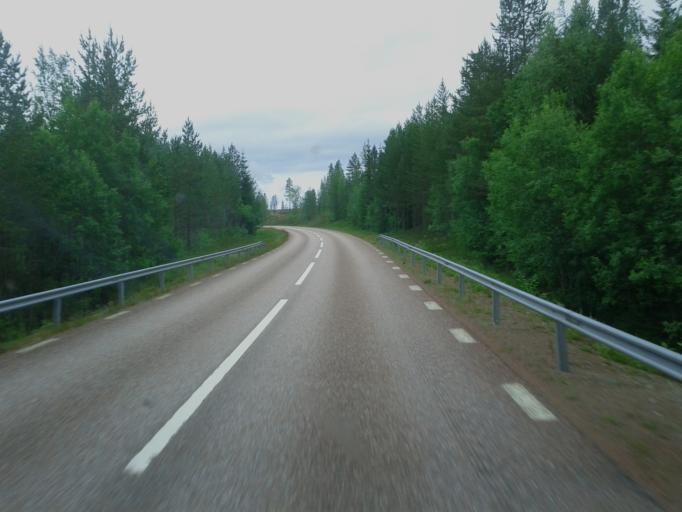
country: NO
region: Hedmark
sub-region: Trysil
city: Innbygda
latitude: 61.7201
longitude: 12.9998
